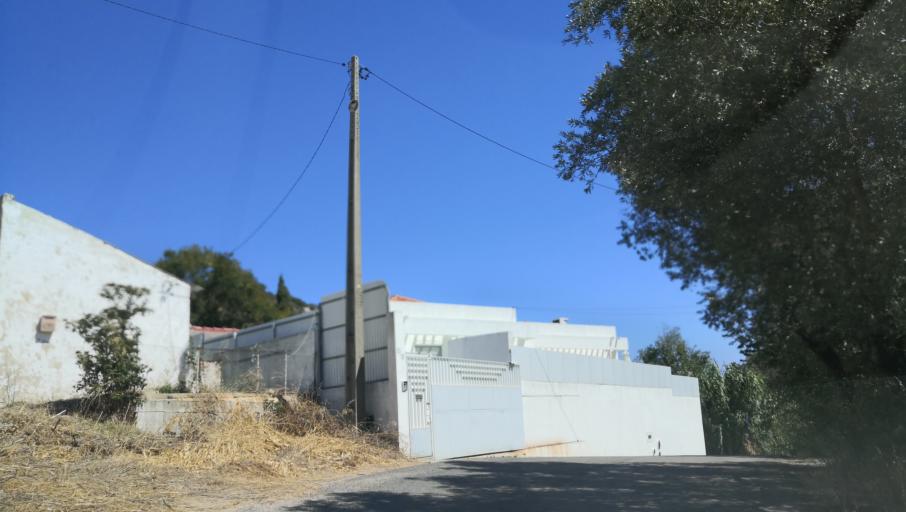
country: PT
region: Setubal
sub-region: Setubal
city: Setubal
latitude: 38.5280
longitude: -8.9235
